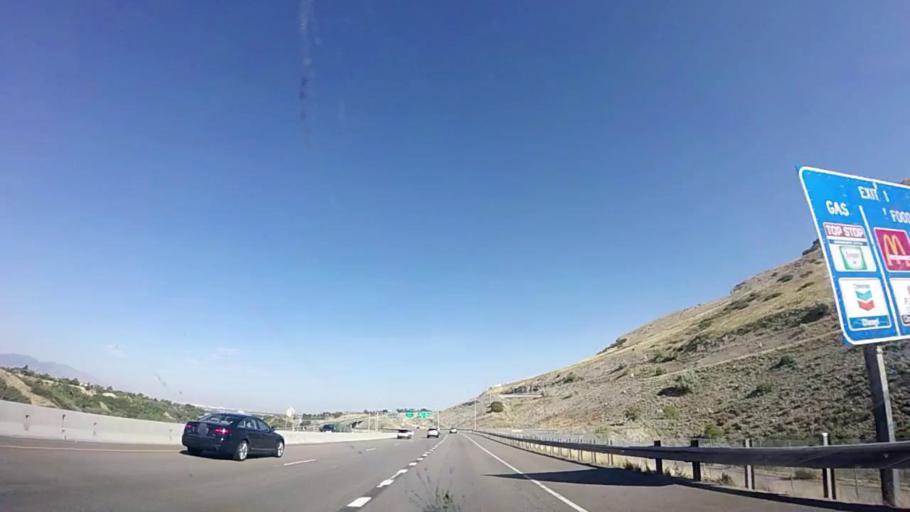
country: US
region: Utah
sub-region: Salt Lake County
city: East Millcreek
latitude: 40.7097
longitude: -111.7997
